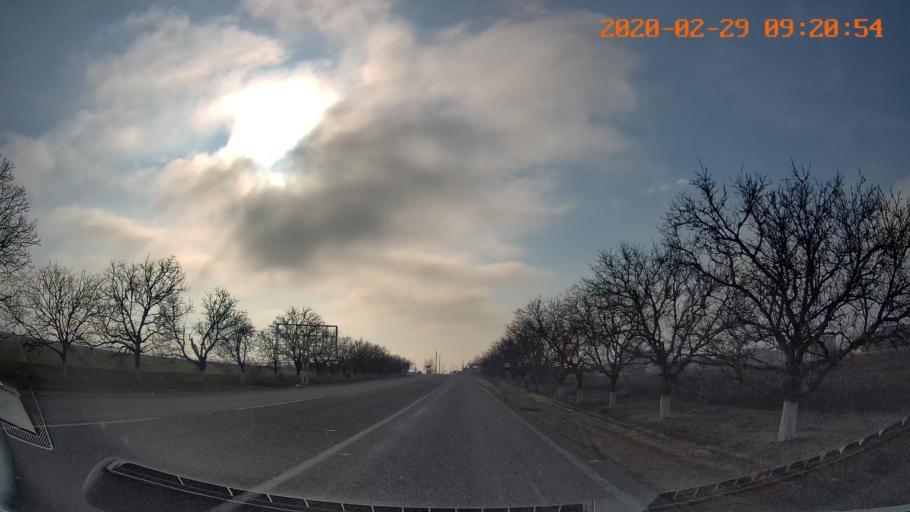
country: MD
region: Telenesti
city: Pervomaisc
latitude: 46.7425
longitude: 29.9534
